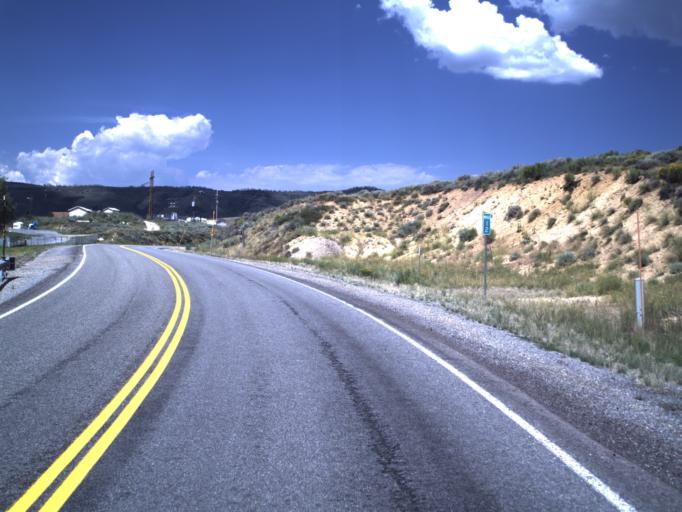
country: US
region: Utah
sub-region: Carbon County
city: Helper
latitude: 39.7908
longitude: -111.1293
